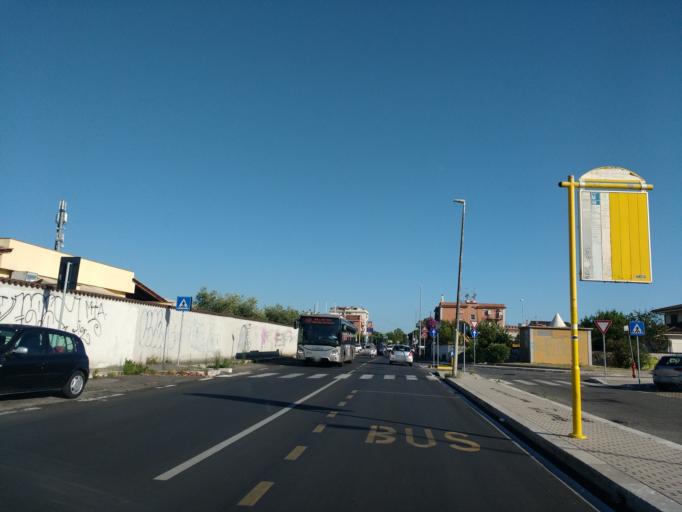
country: IT
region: Latium
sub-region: Citta metropolitana di Roma Capitale
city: Acilia-Castel Fusano-Ostia Antica
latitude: 41.7719
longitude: 12.3549
